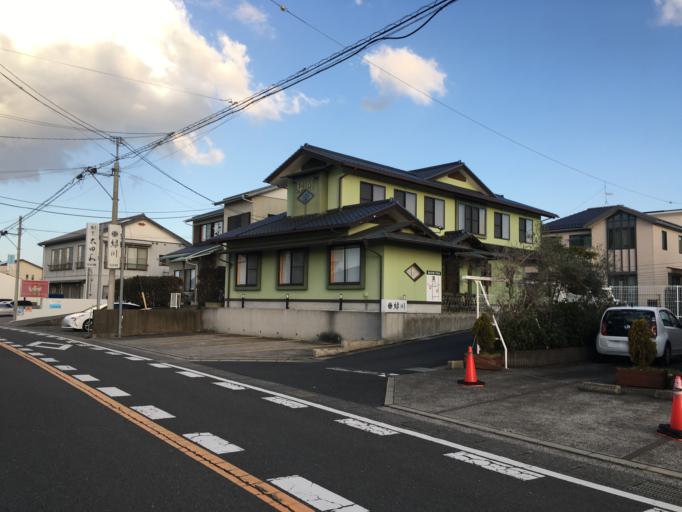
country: JP
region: Chiba
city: Tateyama
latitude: 34.9973
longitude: 139.8670
